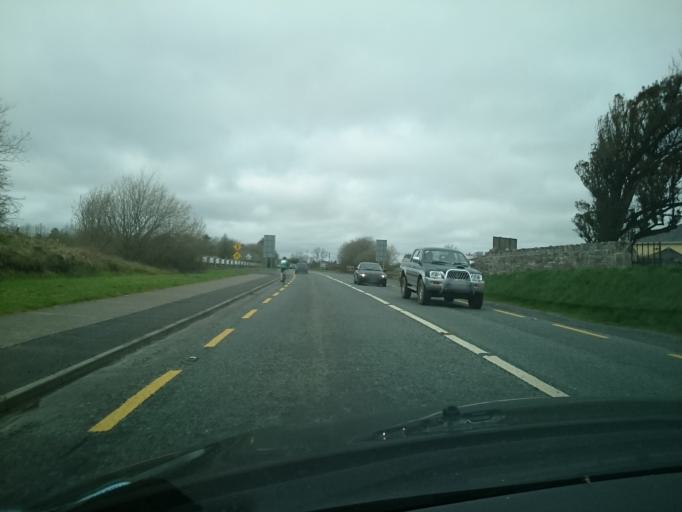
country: IE
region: Connaught
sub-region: Maigh Eo
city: Kiltamagh
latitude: 53.8094
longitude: -9.1374
